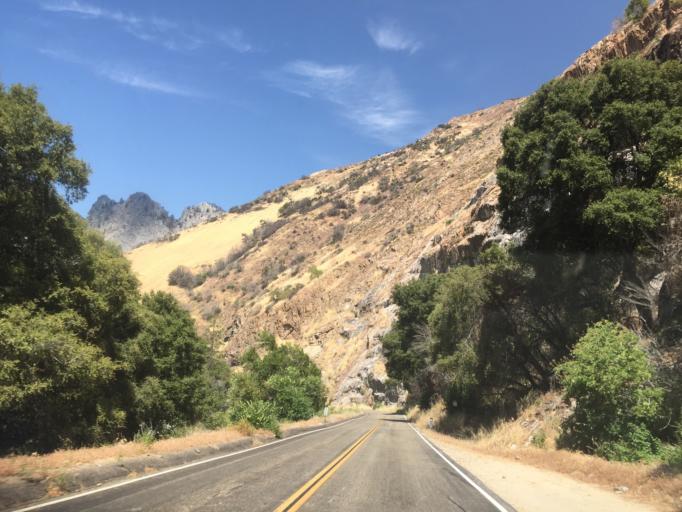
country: US
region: California
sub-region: Tulare County
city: Three Rivers
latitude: 36.8124
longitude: -118.8043
